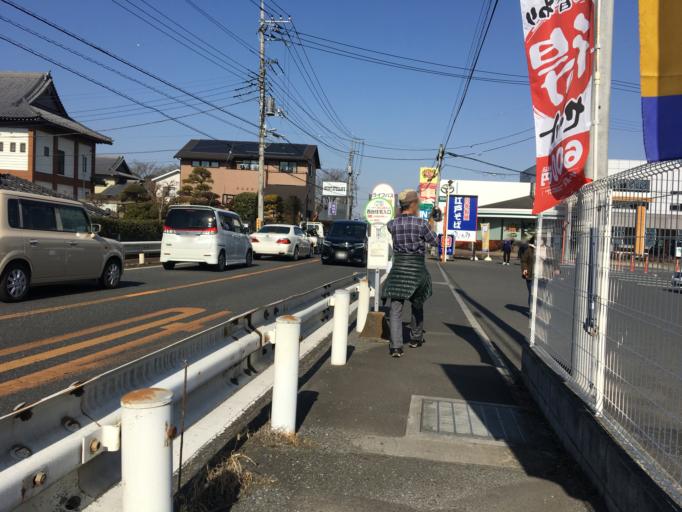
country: JP
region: Saitama
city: Oi
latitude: 35.8488
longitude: 139.5185
